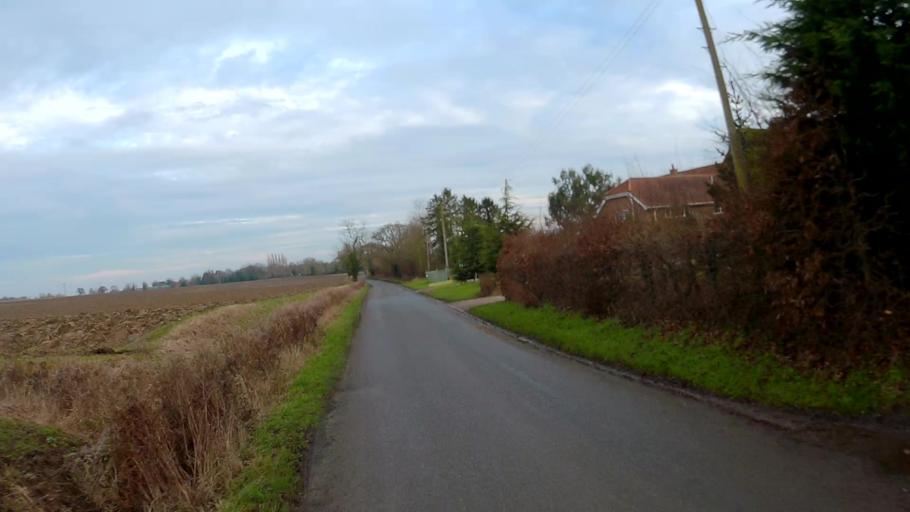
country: GB
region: England
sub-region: Lincolnshire
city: Bourne
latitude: 52.8315
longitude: -0.4208
